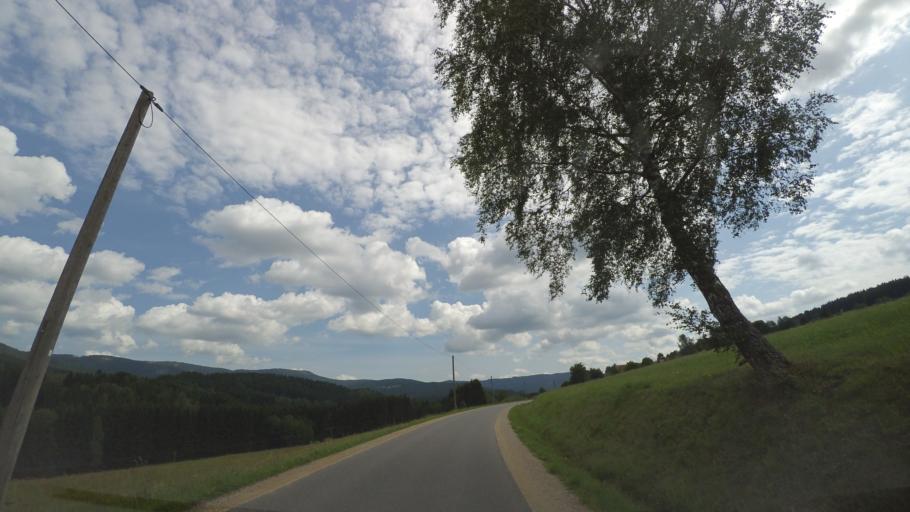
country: DE
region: Bavaria
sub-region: Upper Palatinate
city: Lohberg
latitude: 49.1761
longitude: 13.0751
